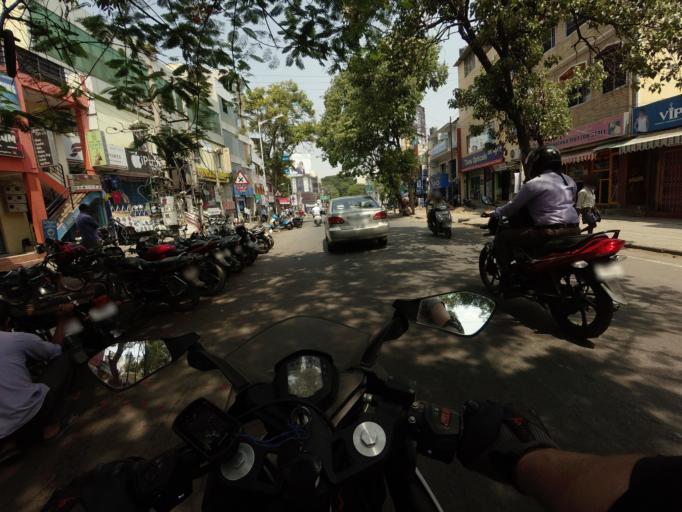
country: IN
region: Karnataka
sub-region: Bangalore Urban
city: Bangalore
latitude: 13.0144
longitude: 77.6365
